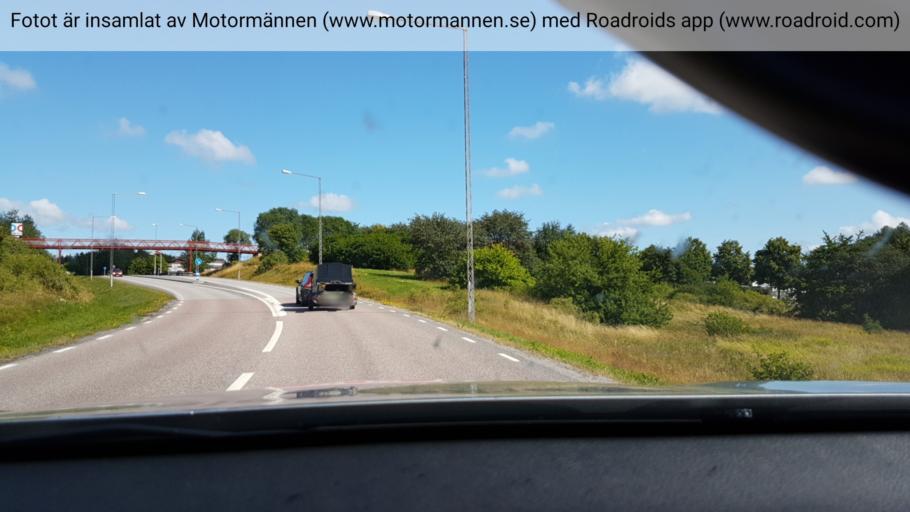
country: SE
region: Stockholm
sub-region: Norrtalje Kommun
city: Norrtalje
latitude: 59.7445
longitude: 18.6908
